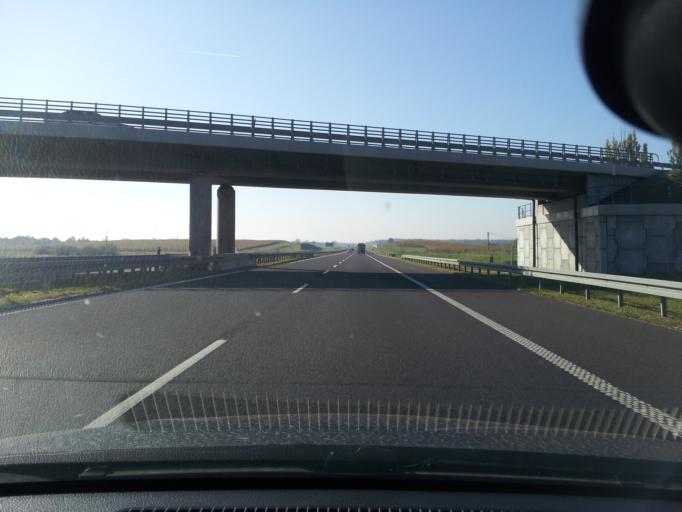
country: PL
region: Kujawsko-Pomorskie
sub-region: Powiat swiecki
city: Warlubie
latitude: 53.5958
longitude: 18.6159
